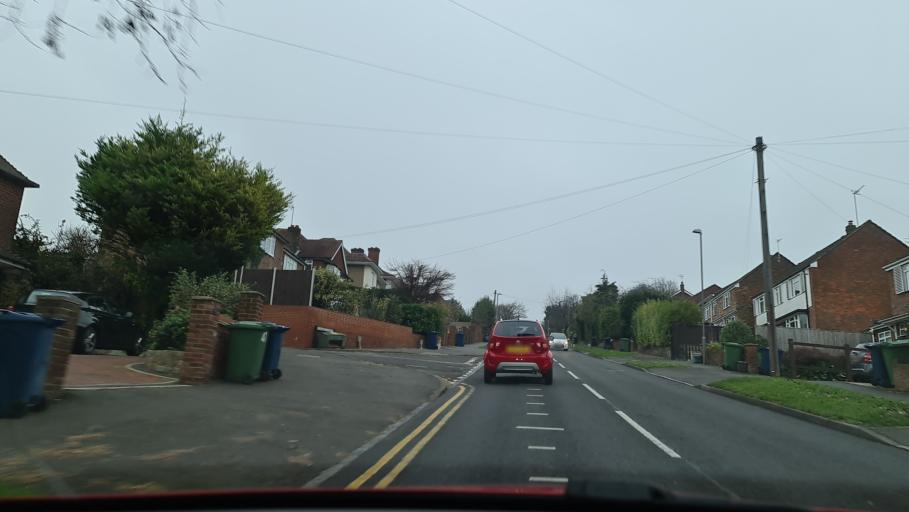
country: GB
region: England
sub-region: Buckinghamshire
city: High Wycombe
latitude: 51.6386
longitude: -0.7451
